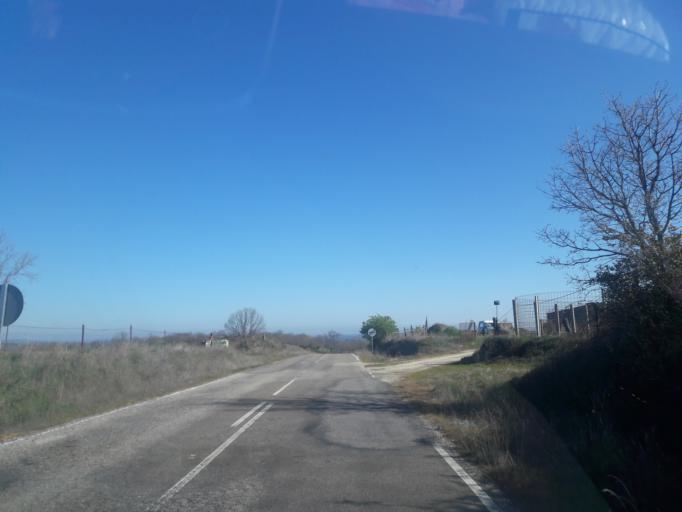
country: ES
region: Castille and Leon
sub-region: Provincia de Salamanca
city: Cabeza del Caballo
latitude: 41.1396
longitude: -6.5580
